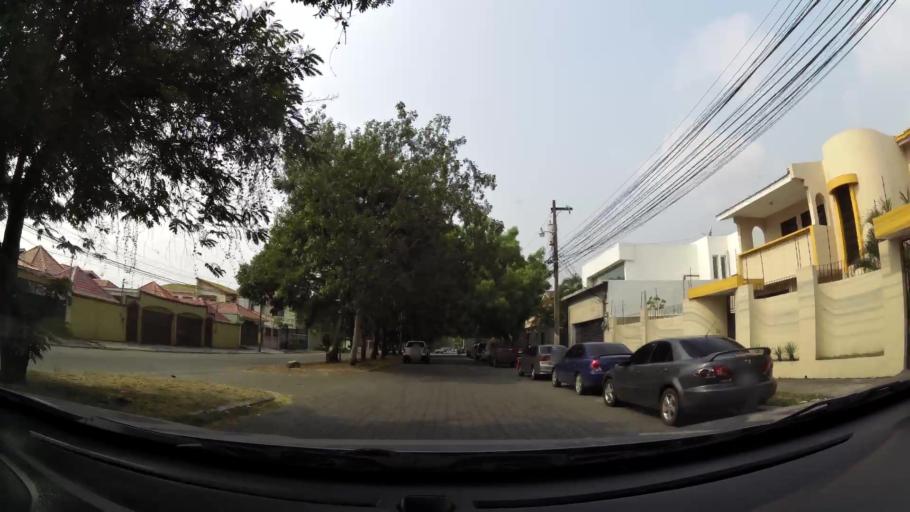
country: HN
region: Cortes
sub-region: San Pedro Sula
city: Pena Blanca
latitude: 15.5370
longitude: -88.0278
